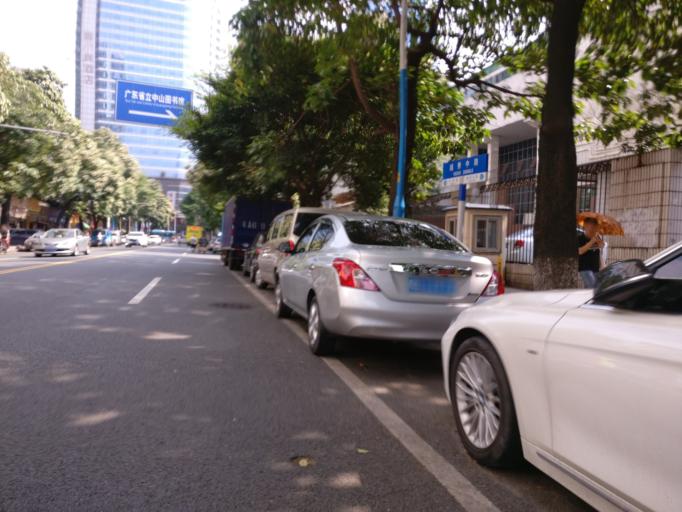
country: CN
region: Guangdong
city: Guangzhou
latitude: 23.1269
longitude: 113.2731
